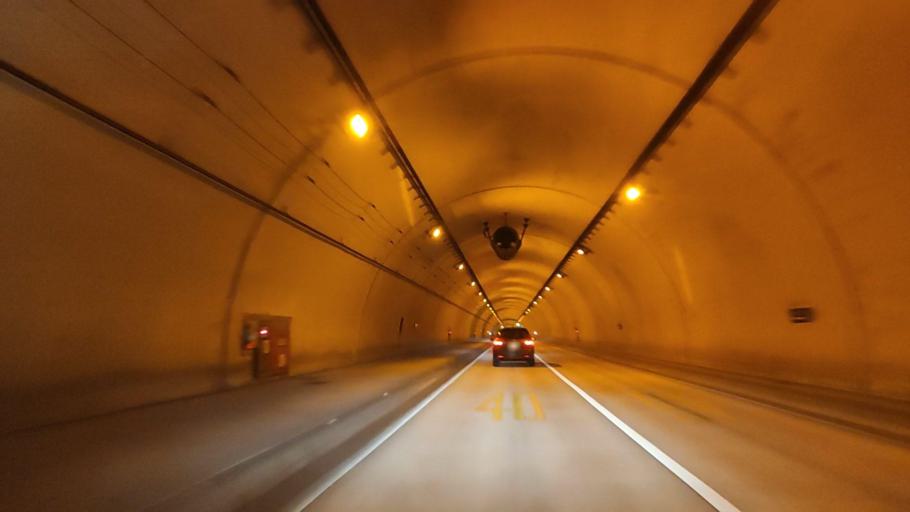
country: JP
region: Ehime
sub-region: Shikoku-chuo Shi
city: Matsuyama
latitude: 33.8784
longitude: 132.7128
